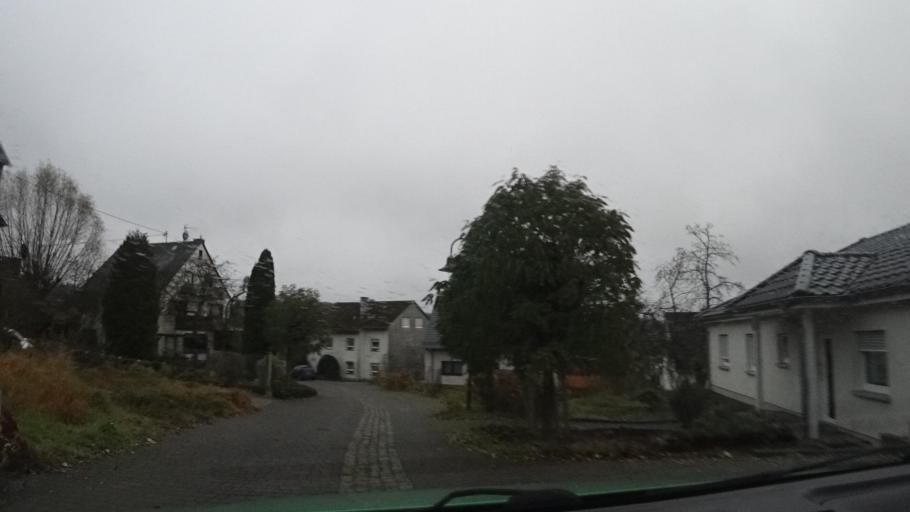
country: DE
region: Rheinland-Pfalz
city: Norath
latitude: 50.1250
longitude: 7.5797
